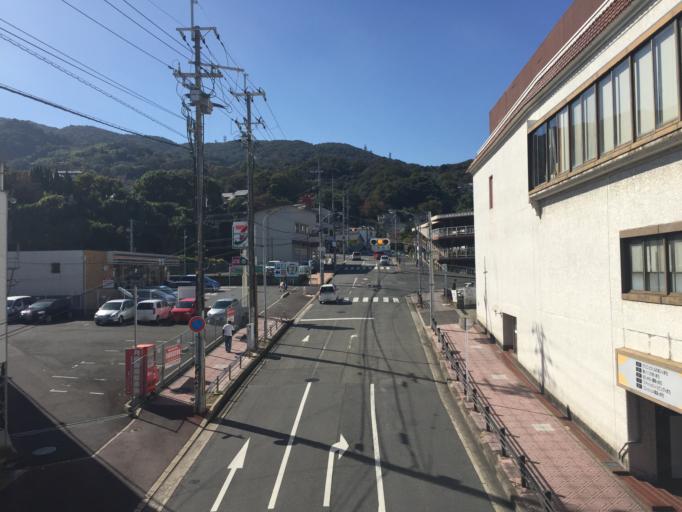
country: JP
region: Nara
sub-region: Ikoma-shi
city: Ikoma
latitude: 34.6926
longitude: 135.6963
